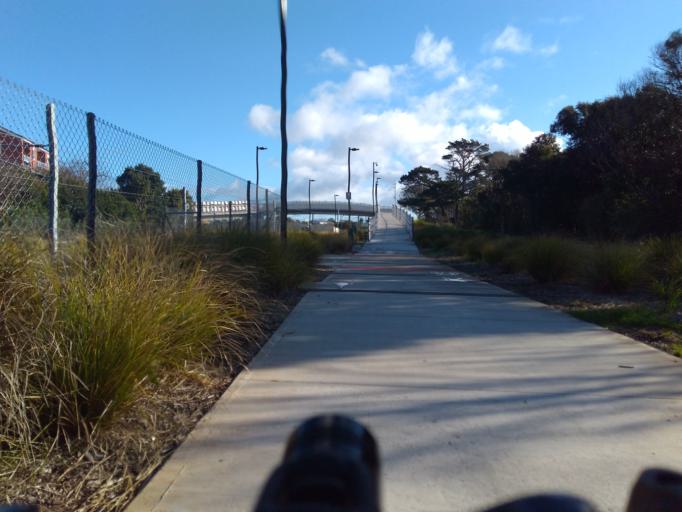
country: NZ
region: Auckland
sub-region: Auckland
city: Rosebank
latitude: -36.8928
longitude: 174.7046
